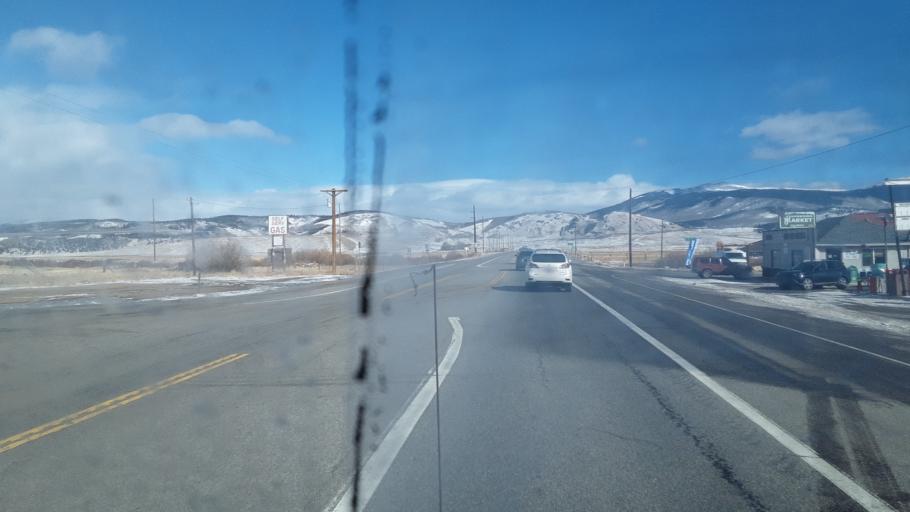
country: US
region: Colorado
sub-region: Park County
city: Fairplay
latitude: 39.3773
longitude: -105.8004
